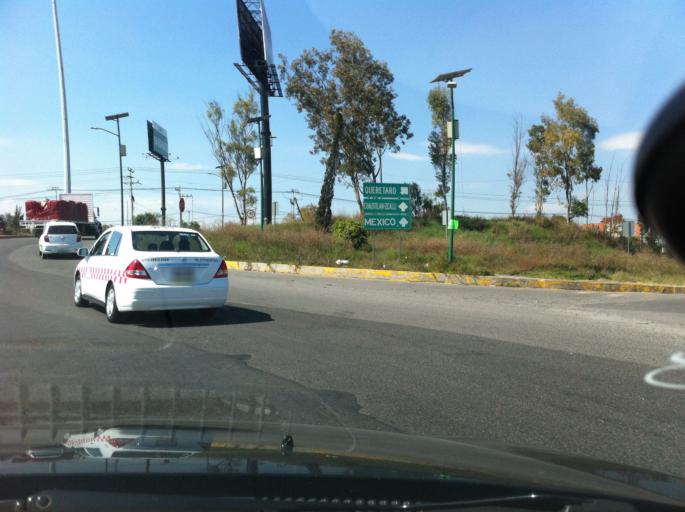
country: MX
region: Mexico
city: Cuautitlan Izcalli
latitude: 19.6450
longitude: -99.1946
